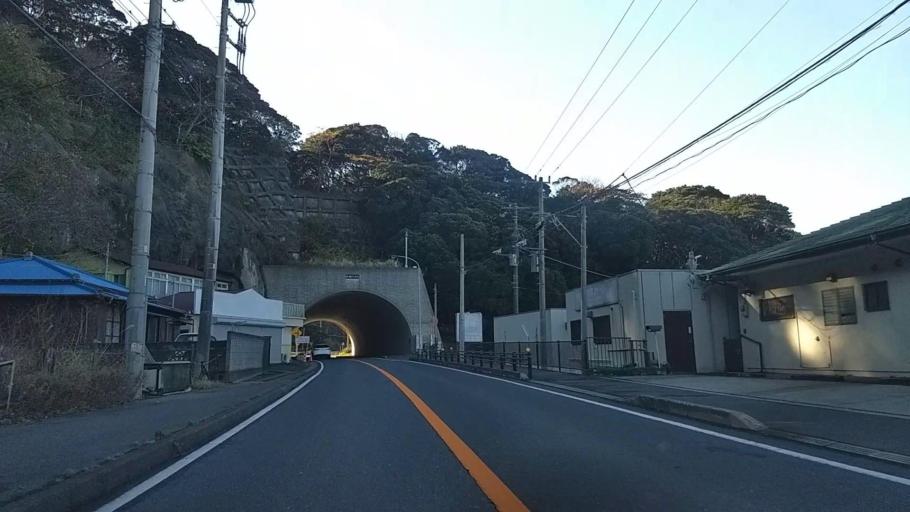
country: JP
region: Chiba
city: Futtsu
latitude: 35.1948
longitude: 139.8234
